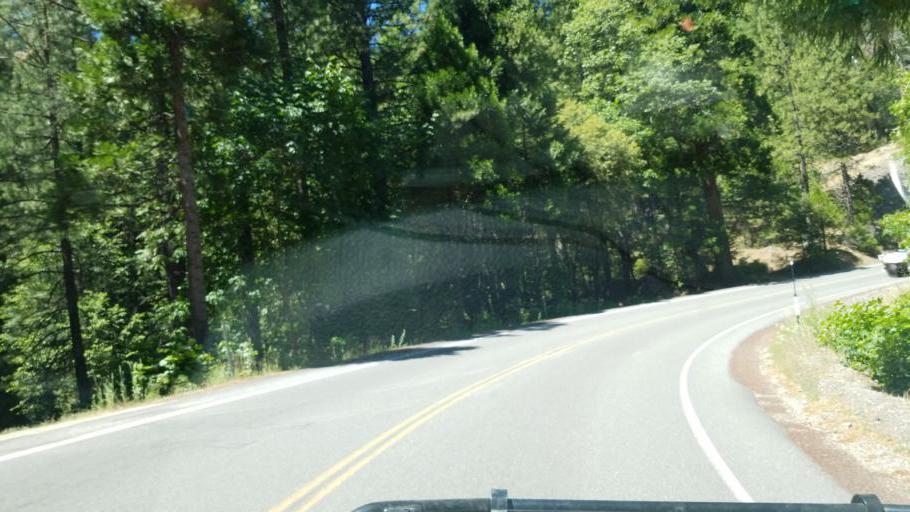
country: US
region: California
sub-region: Butte County
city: Forest Ranch
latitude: 40.1629
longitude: -121.5627
